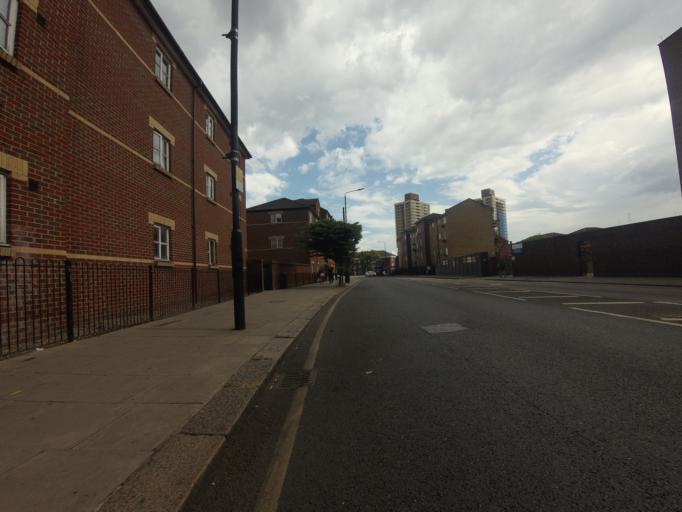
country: GB
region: England
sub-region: Greater London
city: Poplar
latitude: 51.5367
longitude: 0.0066
